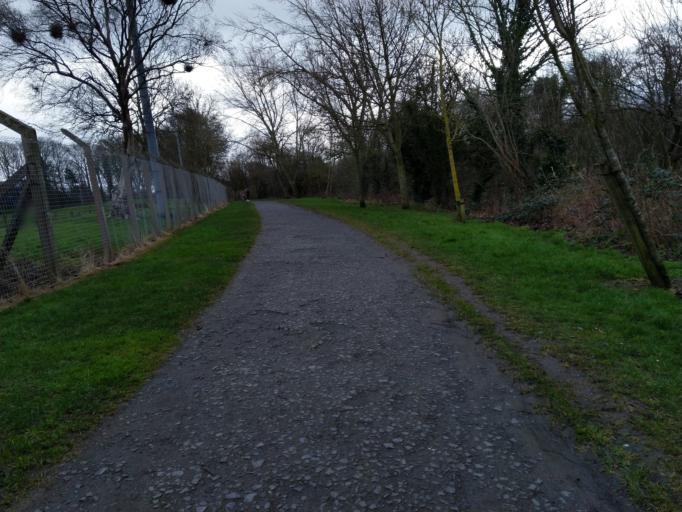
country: GB
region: Scotland
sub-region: South Ayrshire
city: Ayr
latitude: 55.4582
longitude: -4.6207
